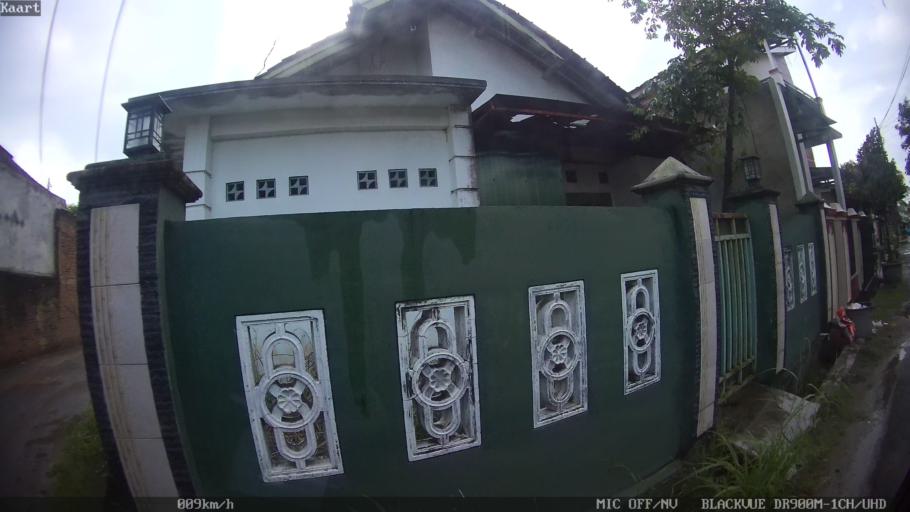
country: ID
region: Lampung
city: Kedaton
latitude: -5.3897
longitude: 105.3022
